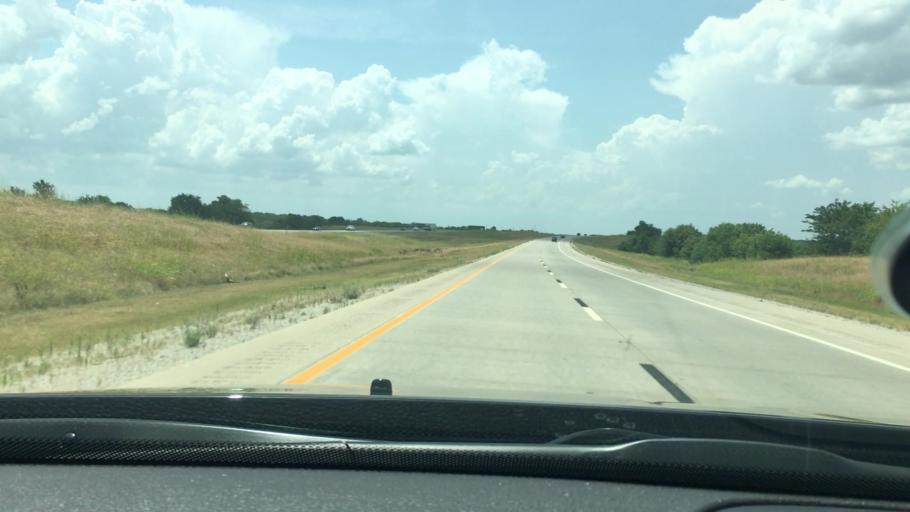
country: US
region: Oklahoma
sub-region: Carter County
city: Ardmore
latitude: 34.1081
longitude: -97.1523
